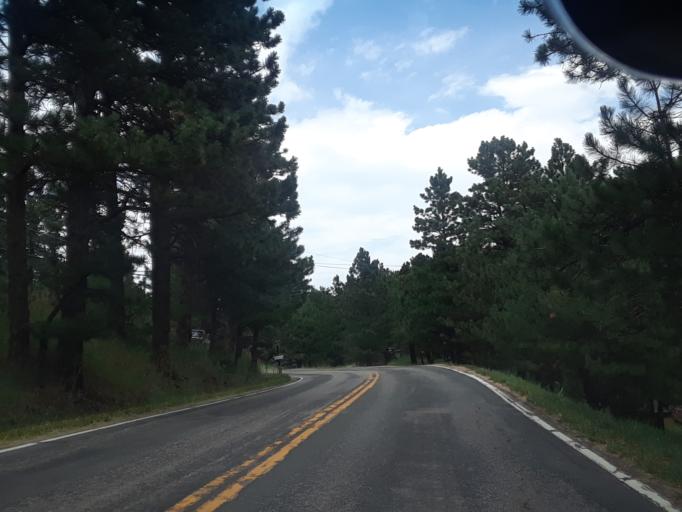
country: US
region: Colorado
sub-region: Boulder County
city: Boulder
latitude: 40.0883
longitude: -105.3021
